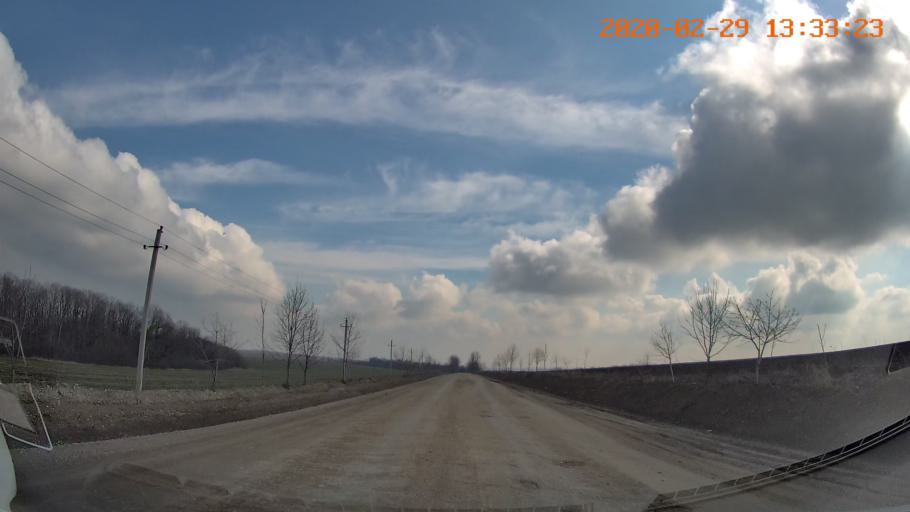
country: MD
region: Telenesti
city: Camenca
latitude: 47.8738
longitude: 28.6161
